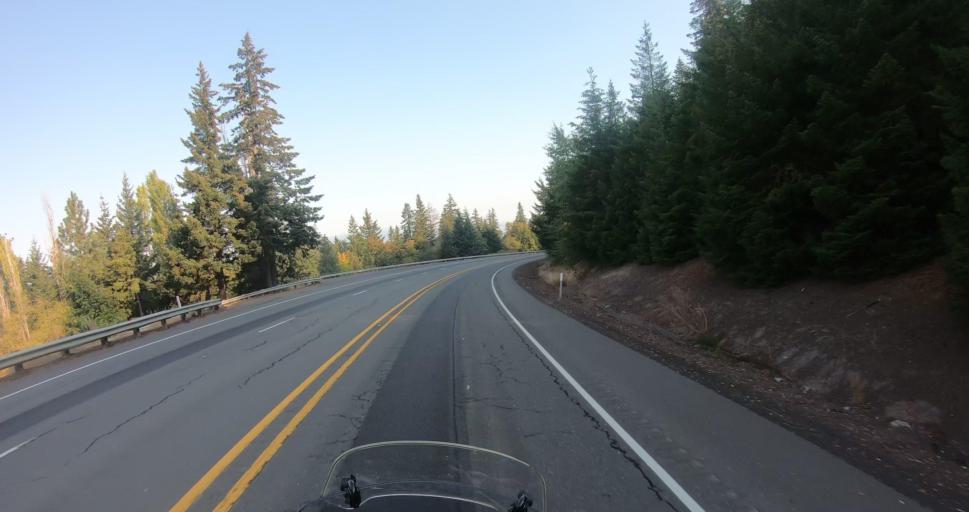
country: US
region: Oregon
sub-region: Hood River County
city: Odell
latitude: 45.5941
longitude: -121.5511
